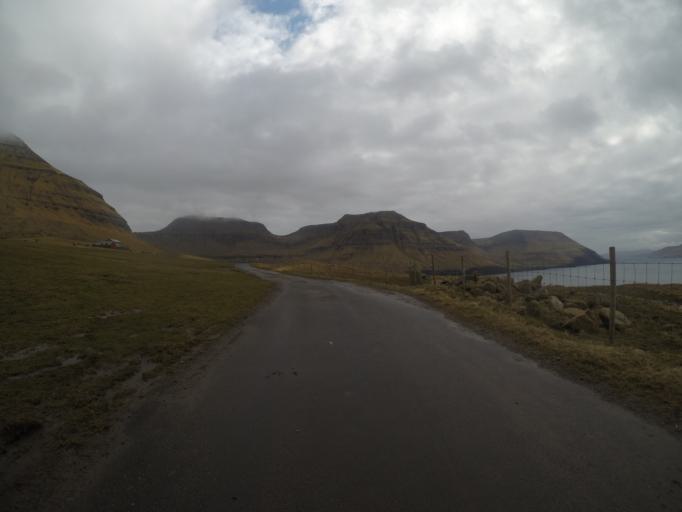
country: FO
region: Streymoy
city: Kollafjordhur
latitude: 62.0401
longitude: -6.9588
